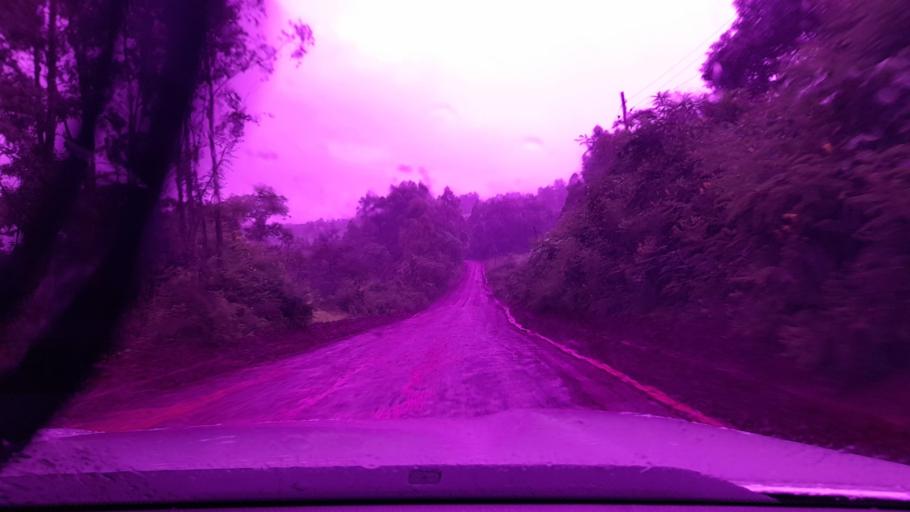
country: ET
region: Oromiya
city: Metu
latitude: 8.3306
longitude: 35.6042
